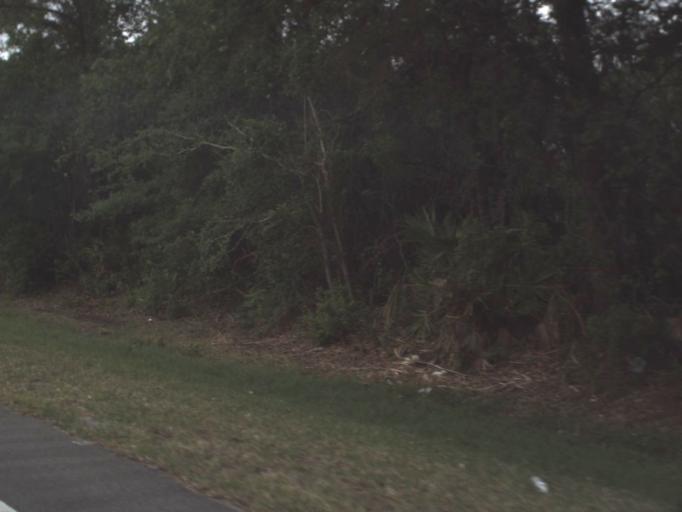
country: US
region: Florida
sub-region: Flagler County
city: Bunnell
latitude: 29.4785
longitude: -81.3385
